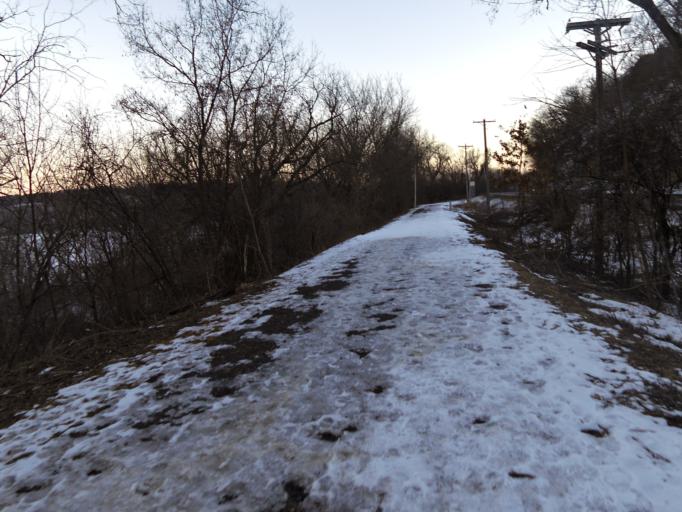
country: US
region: Minnesota
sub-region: Washington County
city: Stillwater
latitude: 45.0721
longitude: -92.8068
